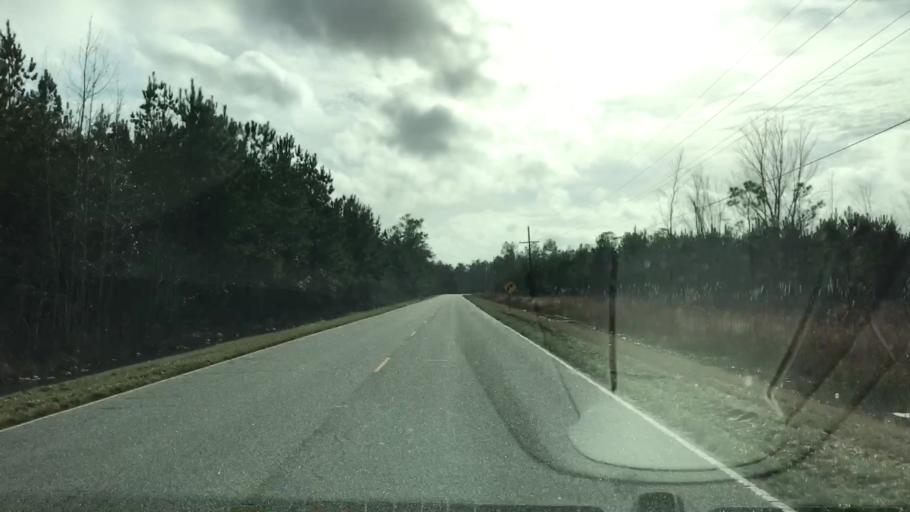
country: US
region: South Carolina
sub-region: Williamsburg County
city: Andrews
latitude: 33.4104
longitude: -79.6079
